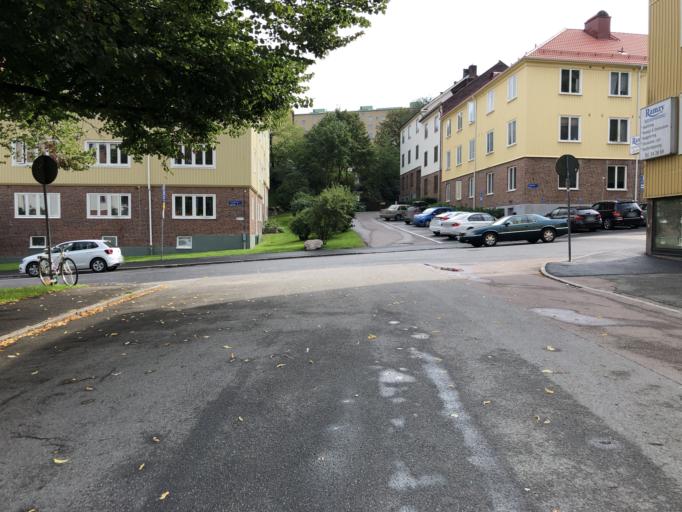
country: SE
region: Vaestra Goetaland
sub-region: Goteborg
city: Majorna
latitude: 57.6906
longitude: 11.9291
